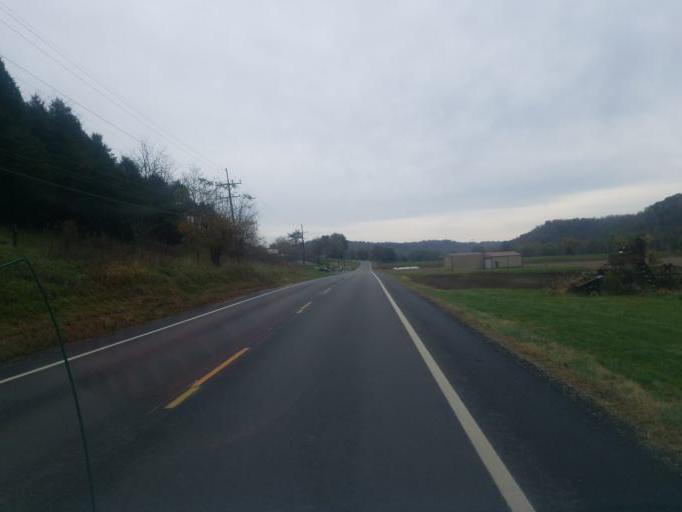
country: US
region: Ohio
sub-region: Washington County
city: Devola
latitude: 39.5250
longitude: -81.4981
